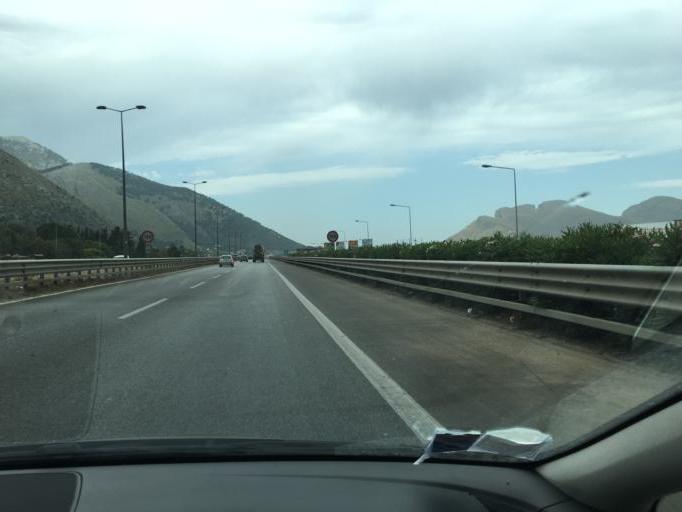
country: IT
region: Sicily
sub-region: Palermo
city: Palermo
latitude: 38.1631
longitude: 13.3087
